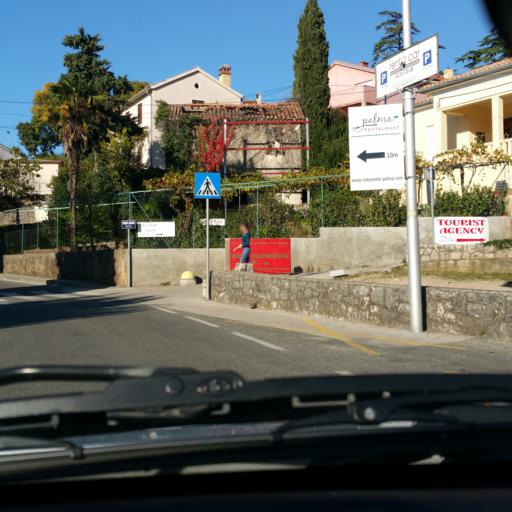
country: HR
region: Primorsko-Goranska
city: Njivice
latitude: 45.1242
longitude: 14.5289
